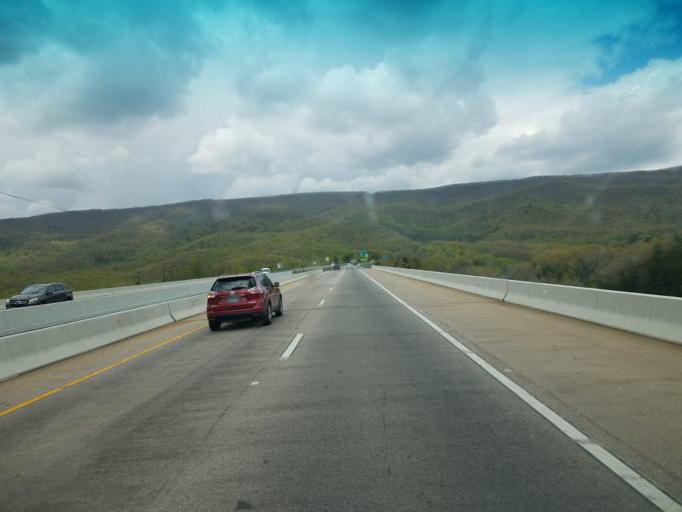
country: US
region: West Virginia
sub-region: Mercer County
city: Bluefield
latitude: 37.2547
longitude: -81.1182
